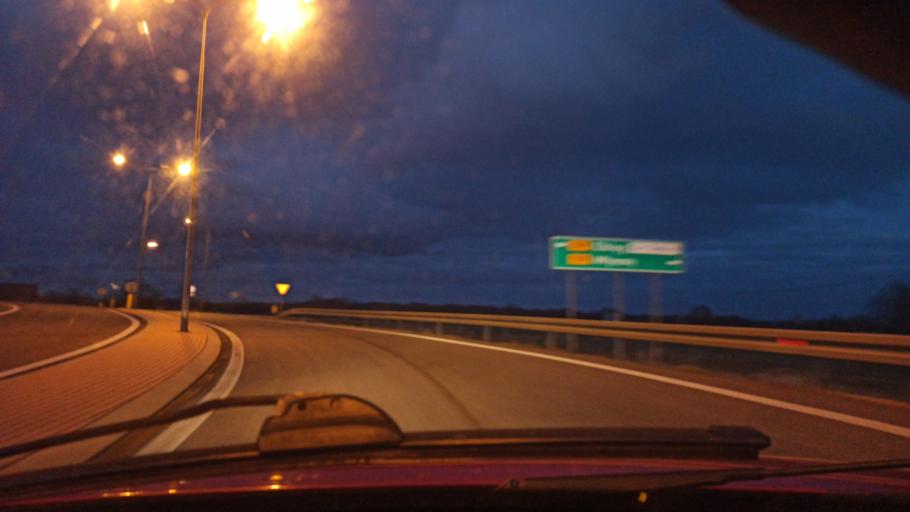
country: PL
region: Warmian-Masurian Voivodeship
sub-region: Powiat elblaski
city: Gronowo Gorne
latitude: 54.1681
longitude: 19.5305
